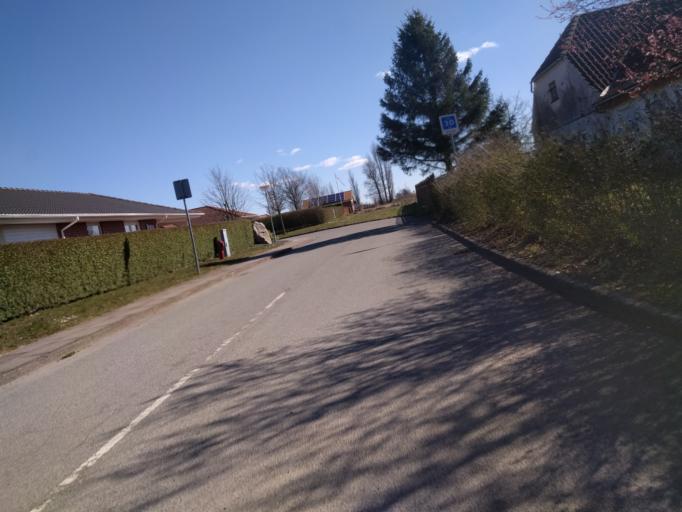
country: DK
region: South Denmark
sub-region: Kerteminde Kommune
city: Langeskov
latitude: 55.3779
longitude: 10.5601
